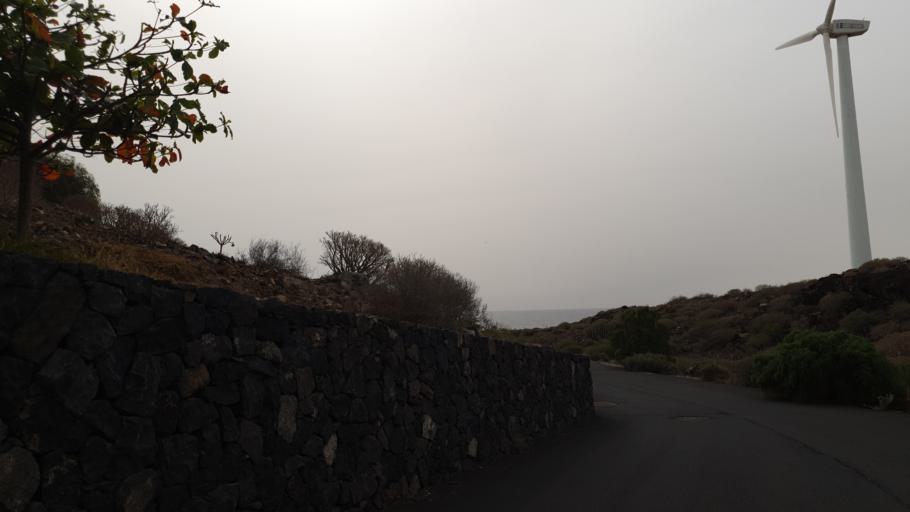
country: ES
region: Canary Islands
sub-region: Provincia de Santa Cruz de Tenerife
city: San Isidro
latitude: 28.0692
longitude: -16.5126
